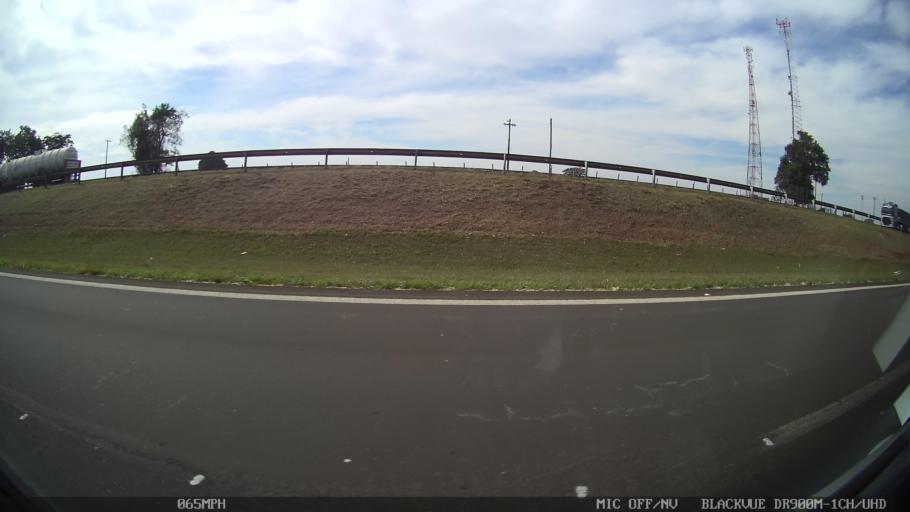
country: BR
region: Sao Paulo
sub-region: Matao
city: Matao
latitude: -21.5972
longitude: -48.4362
